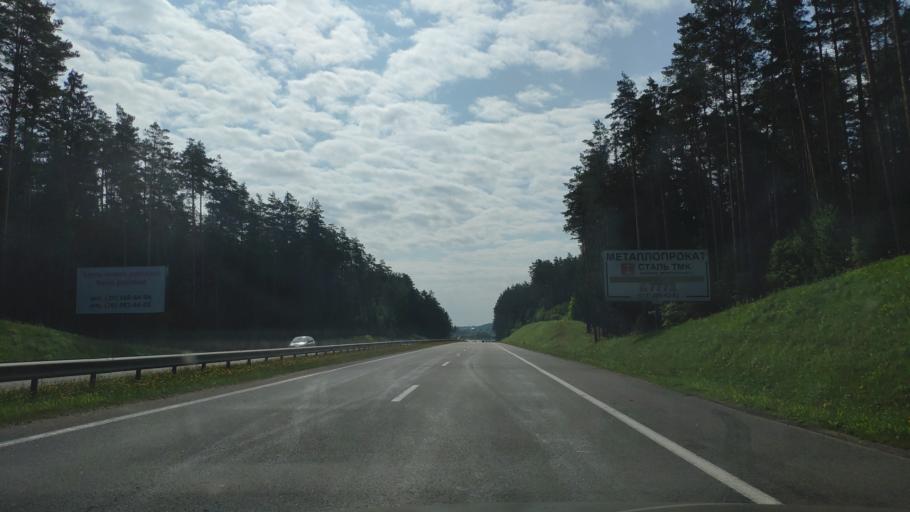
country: BY
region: Minsk
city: Khatsyezhyna
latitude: 53.9577
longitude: 27.3203
